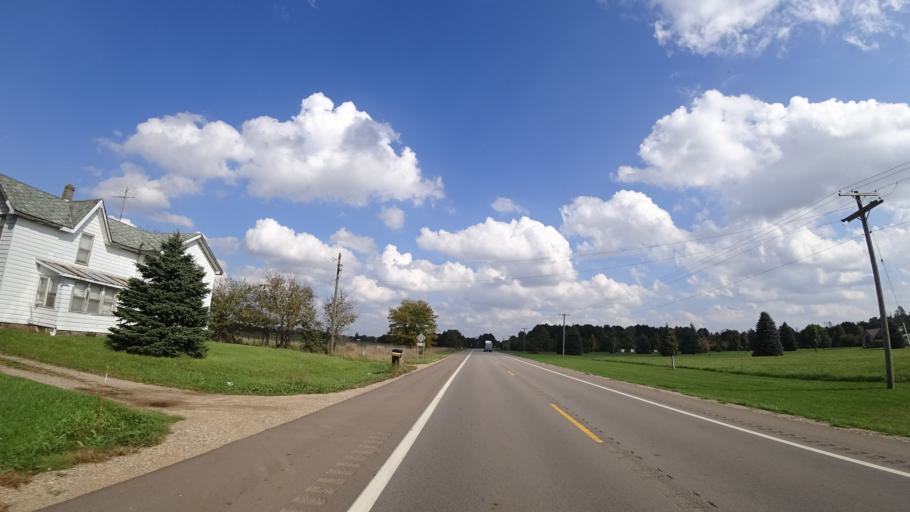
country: US
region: Michigan
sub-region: Branch County
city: Union City
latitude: 42.0682
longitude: -85.1758
